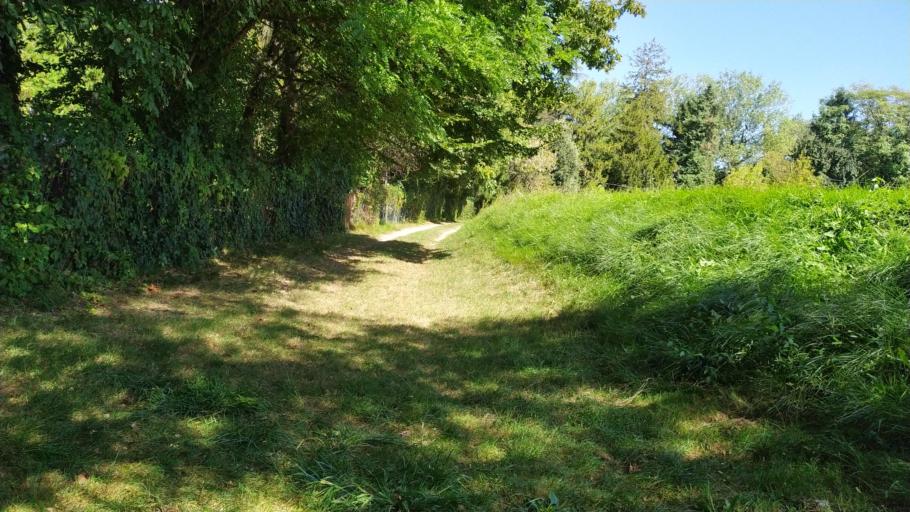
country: IT
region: Friuli Venezia Giulia
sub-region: Provincia di Pordenone
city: Cavolano-Schiavoi
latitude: 45.9382
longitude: 12.4881
